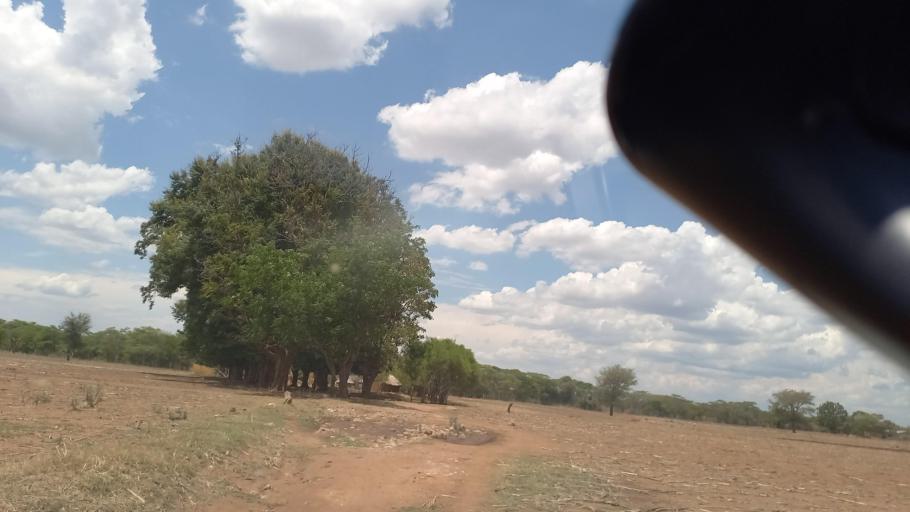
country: ZM
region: Southern
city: Mazabuka
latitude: -16.1111
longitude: 27.8150
